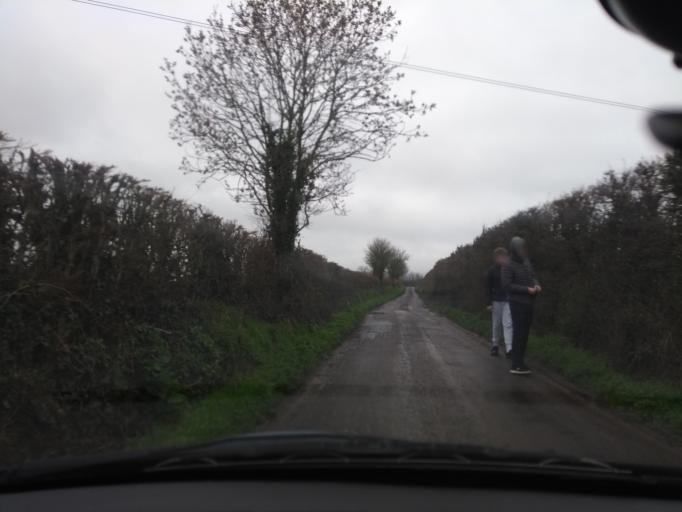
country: GB
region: England
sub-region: Somerset
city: Taunton
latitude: 51.0421
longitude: -3.1206
